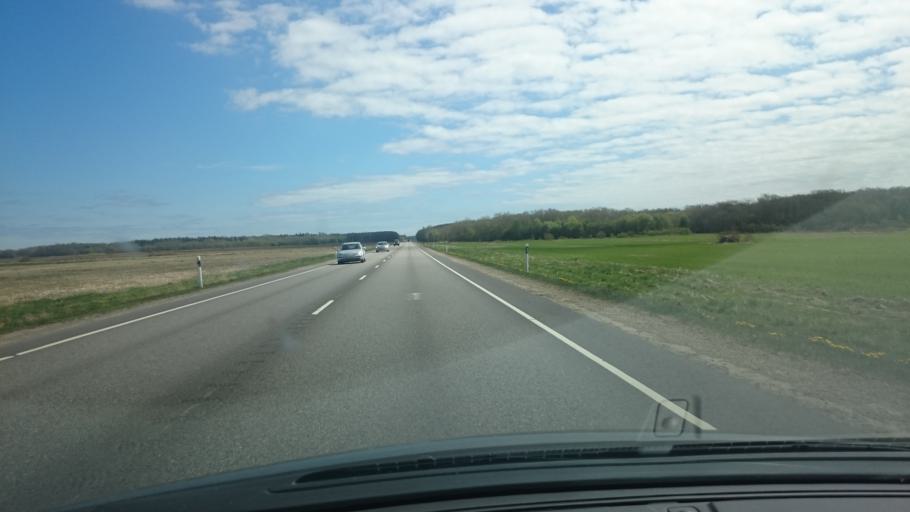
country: EE
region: Ida-Virumaa
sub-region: Kohtla-Jaerve linn
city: Kohtla-Jarve
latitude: 59.4209
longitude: 27.2271
